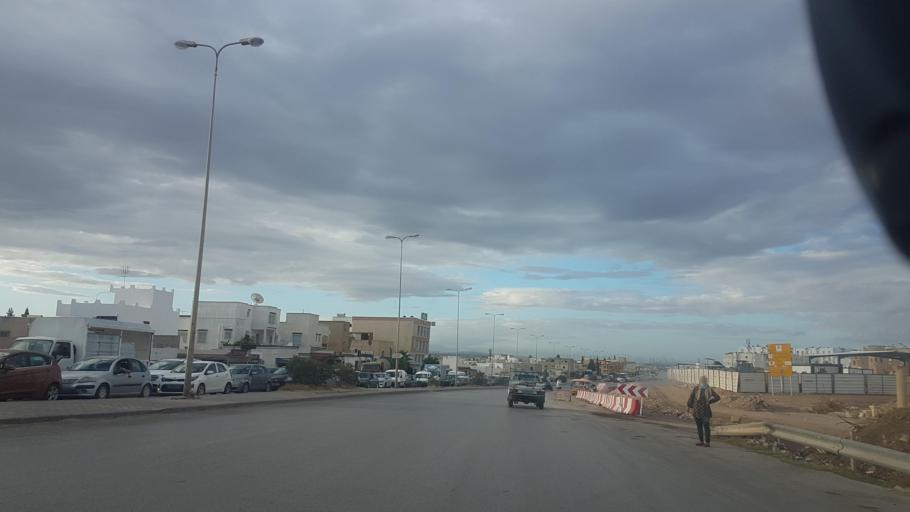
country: TN
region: Bin 'Arus
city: Ben Arous
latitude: 36.7434
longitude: 10.2078
